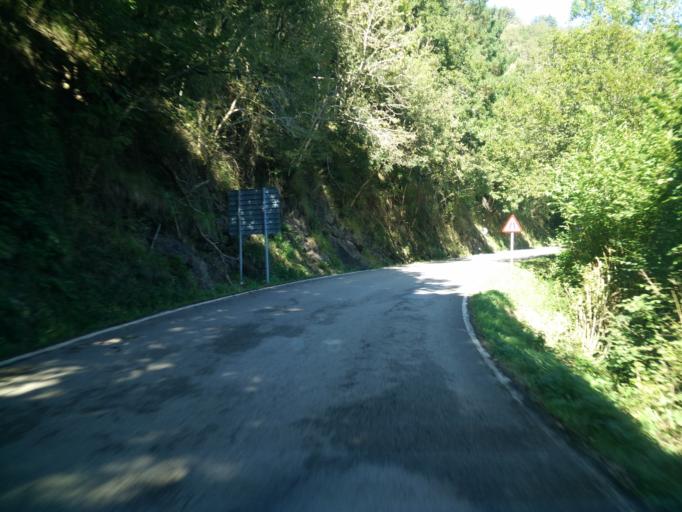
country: ES
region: Cantabria
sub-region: Provincia de Cantabria
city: Ruente
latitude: 43.1467
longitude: -4.2876
